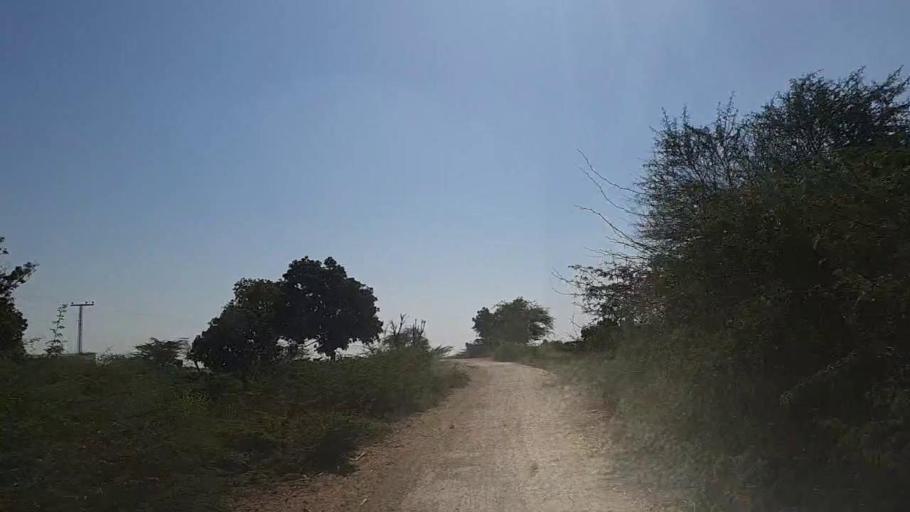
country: PK
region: Sindh
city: Naukot
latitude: 25.0105
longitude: 69.3776
